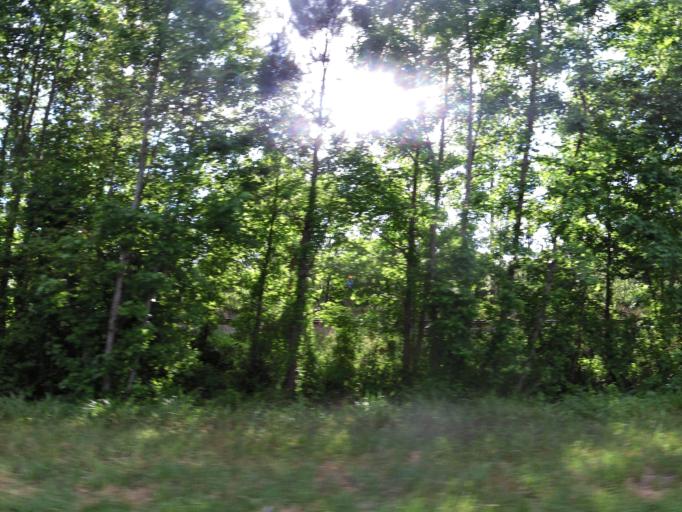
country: US
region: South Carolina
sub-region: Hampton County
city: Estill
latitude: 32.7007
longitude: -81.2426
